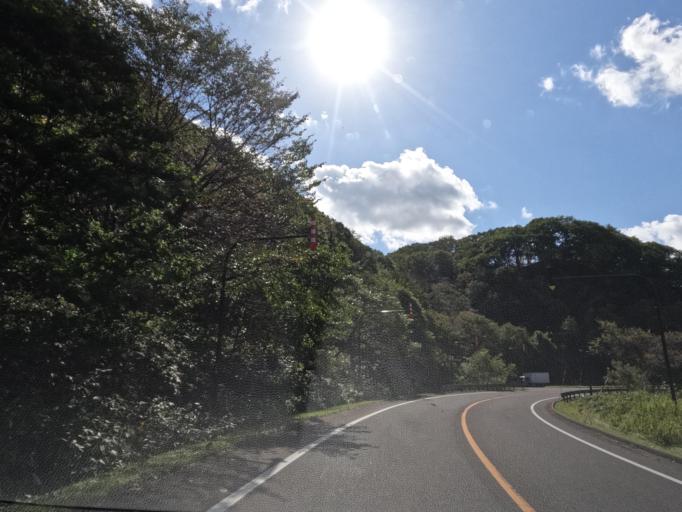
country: JP
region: Hokkaido
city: Shiraoi
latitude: 42.4830
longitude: 141.1460
